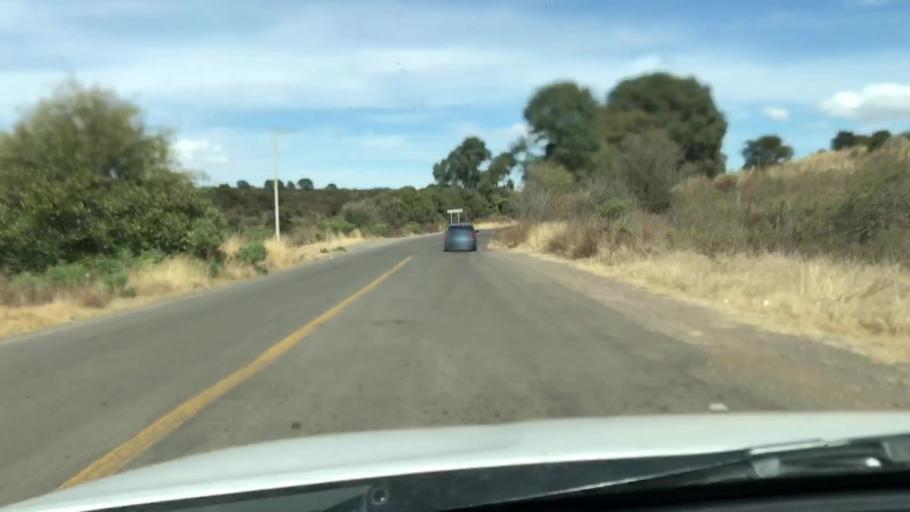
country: MX
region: Jalisco
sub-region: Zacoalco de Torres
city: Barranca de Otates (Barranca de Otatan)
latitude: 20.1924
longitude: -103.7209
